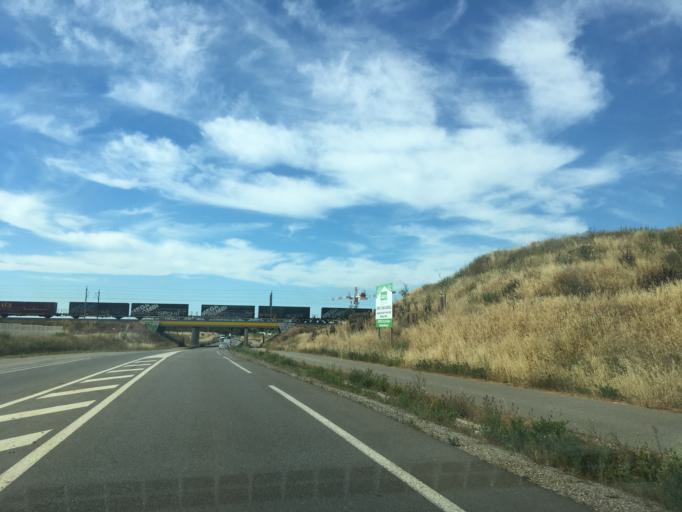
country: FR
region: Languedoc-Roussillon
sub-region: Departement du Gard
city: Bouillargues
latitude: 43.7851
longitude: 4.4298
